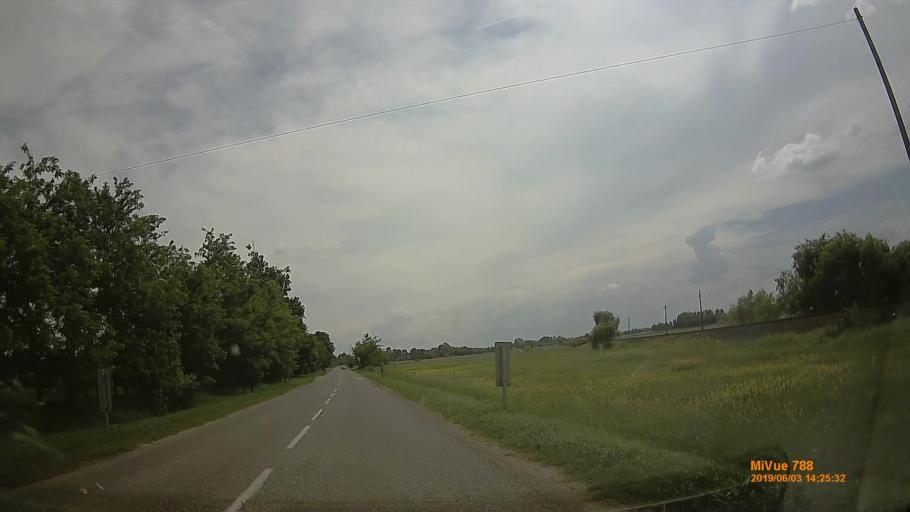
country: HU
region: Bacs-Kiskun
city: Tiszakecske
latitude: 47.0031
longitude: 20.1257
